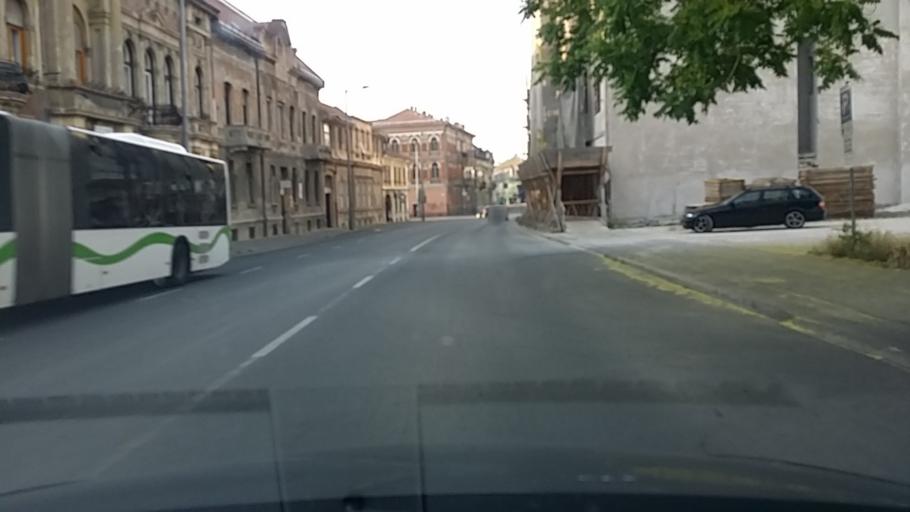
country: HU
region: Borsod-Abauj-Zemplen
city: Miskolc
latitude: 48.0999
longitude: 20.7852
